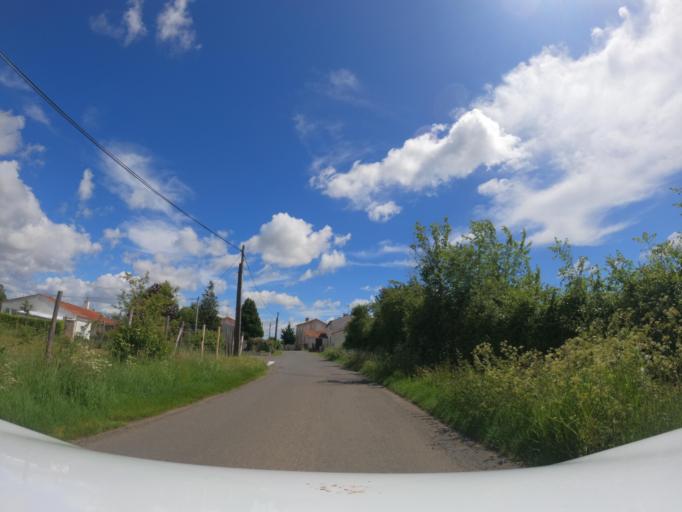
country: FR
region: Pays de la Loire
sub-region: Departement de la Vendee
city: Le Champ-Saint-Pere
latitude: 46.4918
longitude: -1.3362
